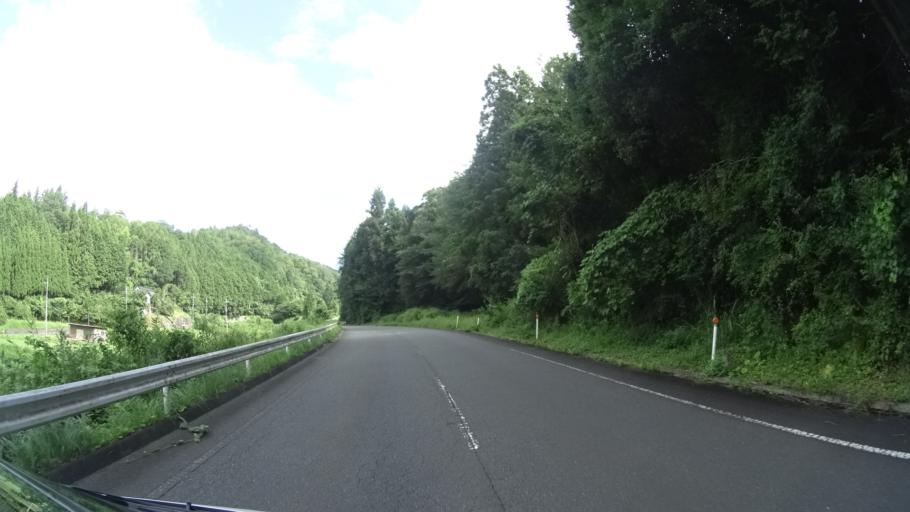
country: JP
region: Kyoto
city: Fukuchiyama
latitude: 35.3538
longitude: 135.1495
